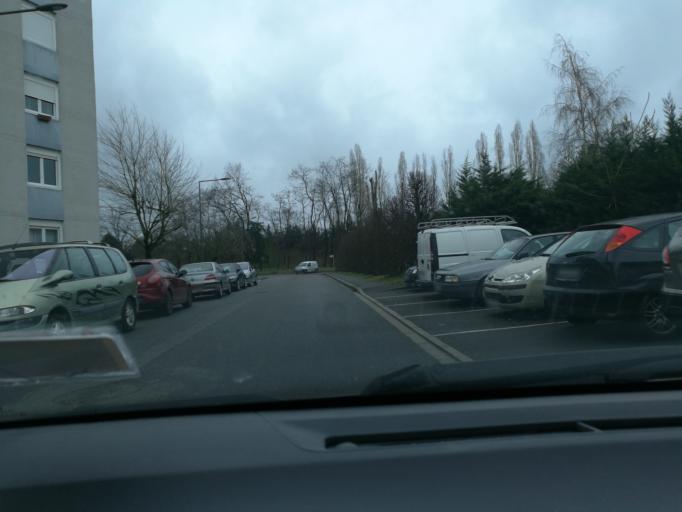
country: FR
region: Centre
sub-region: Departement du Loiret
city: Fleury-les-Aubrais
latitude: 47.9384
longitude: 1.9127
